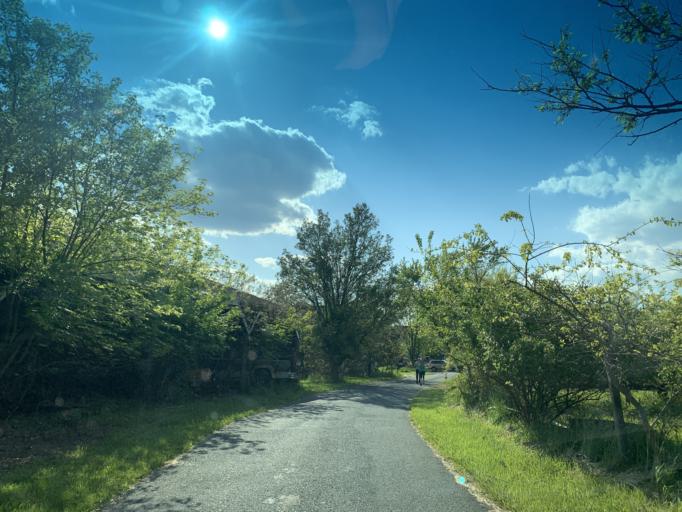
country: US
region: Maryland
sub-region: Baltimore County
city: White Marsh
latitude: 39.4042
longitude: -76.4375
